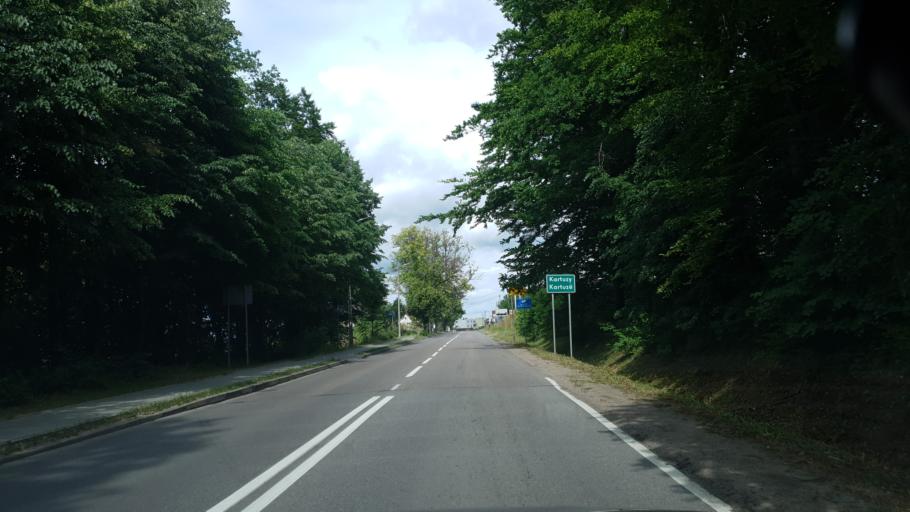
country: PL
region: Pomeranian Voivodeship
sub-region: Powiat kartuski
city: Kartuzy
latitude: 54.3205
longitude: 18.1836
